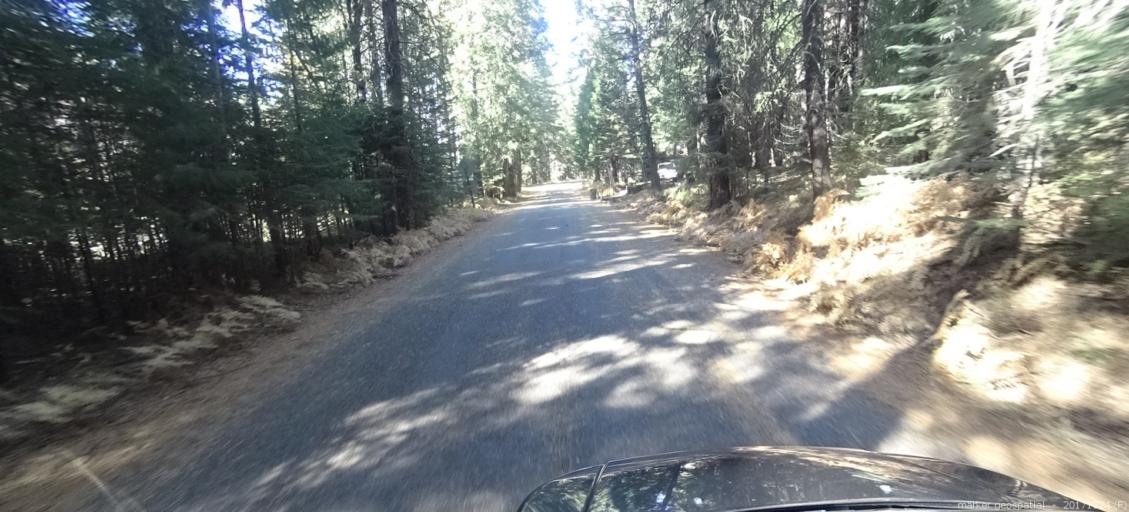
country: US
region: California
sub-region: Shasta County
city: Shingletown
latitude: 40.5152
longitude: -121.6757
